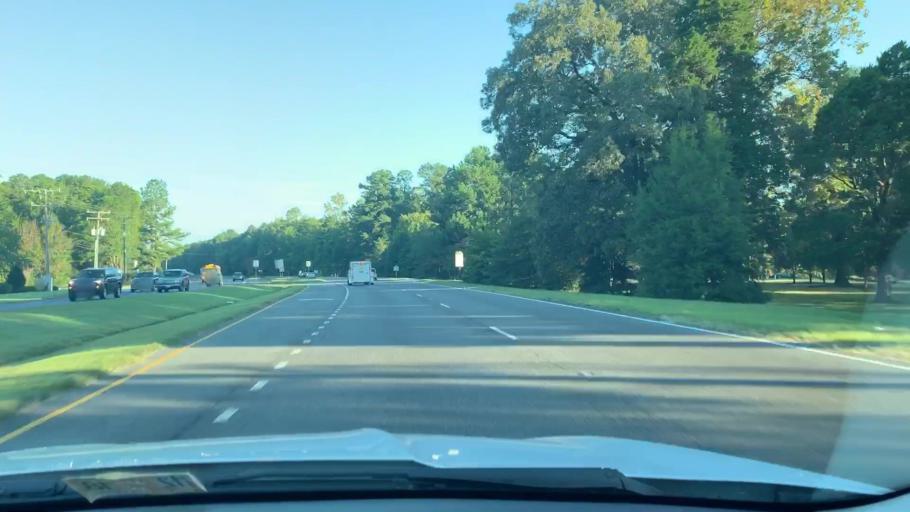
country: US
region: Virginia
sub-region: Gloucester County
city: Gloucester Courthouse
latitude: 37.3325
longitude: -76.5144
